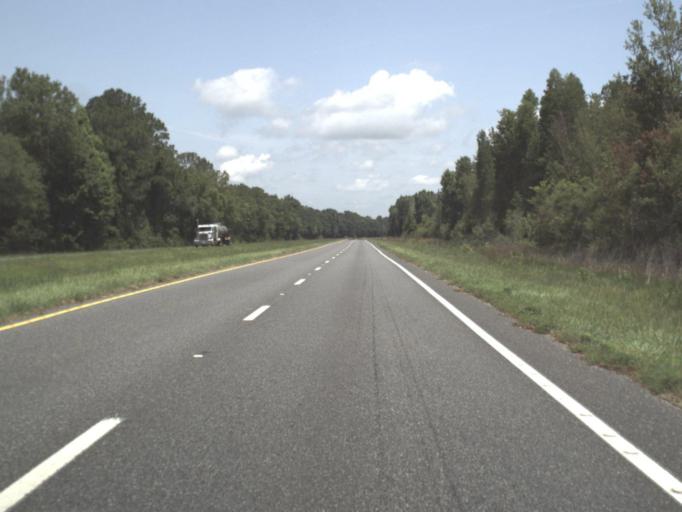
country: US
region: Florida
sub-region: Taylor County
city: Perry
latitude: 29.9249
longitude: -83.4398
